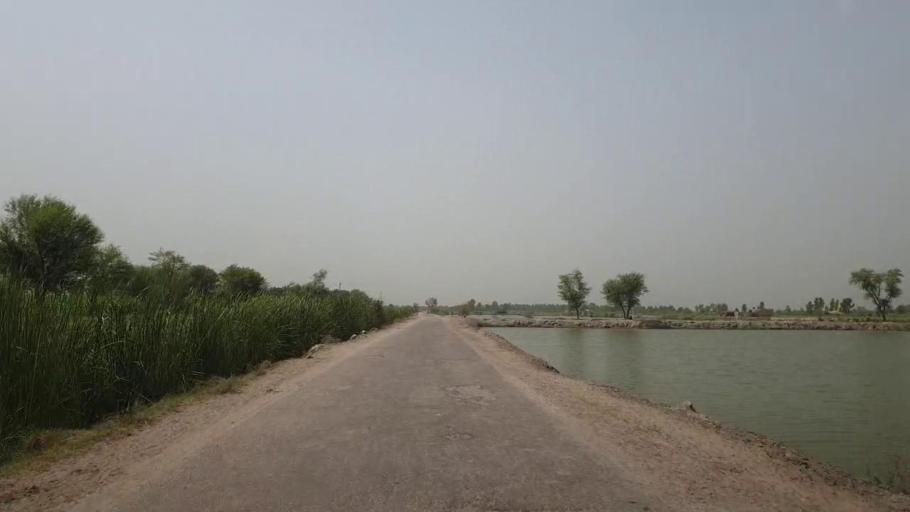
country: PK
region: Sindh
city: Gambat
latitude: 27.3932
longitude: 68.5509
